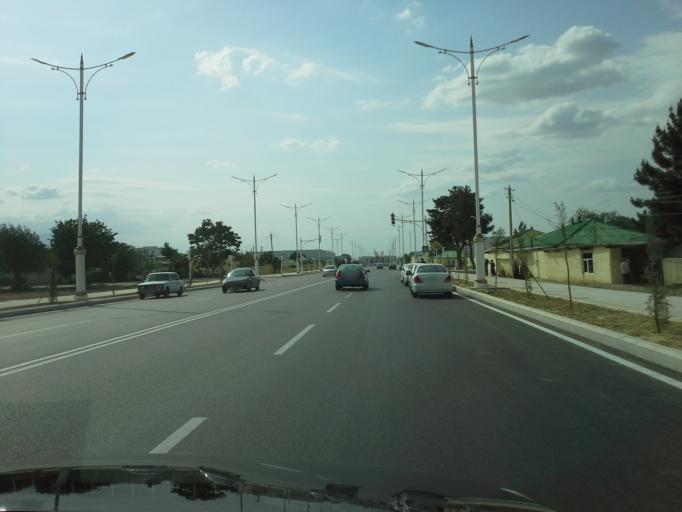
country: TM
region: Ahal
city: Ashgabat
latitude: 37.9605
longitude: 58.3362
